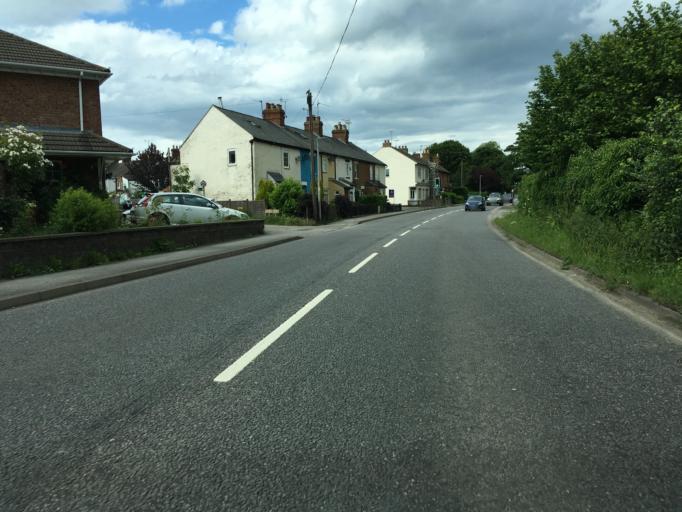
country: GB
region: England
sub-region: Buckinghamshire
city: Stewkley
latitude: 51.8960
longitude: -0.7163
